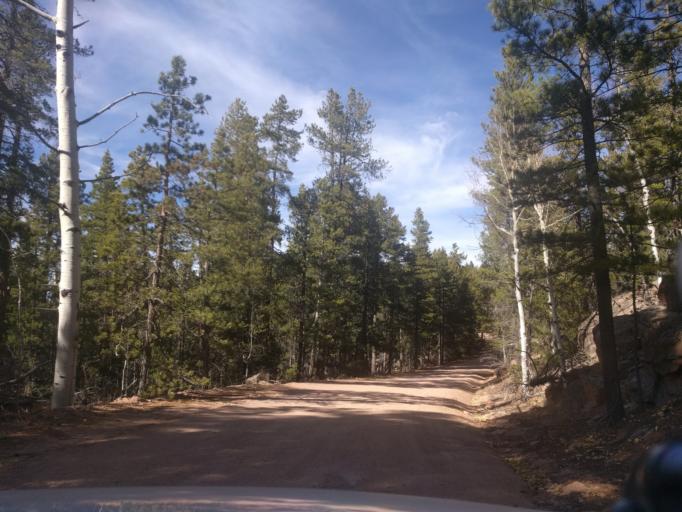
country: US
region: Colorado
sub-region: Douglas County
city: Perry Park
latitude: 39.2142
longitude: -105.0581
